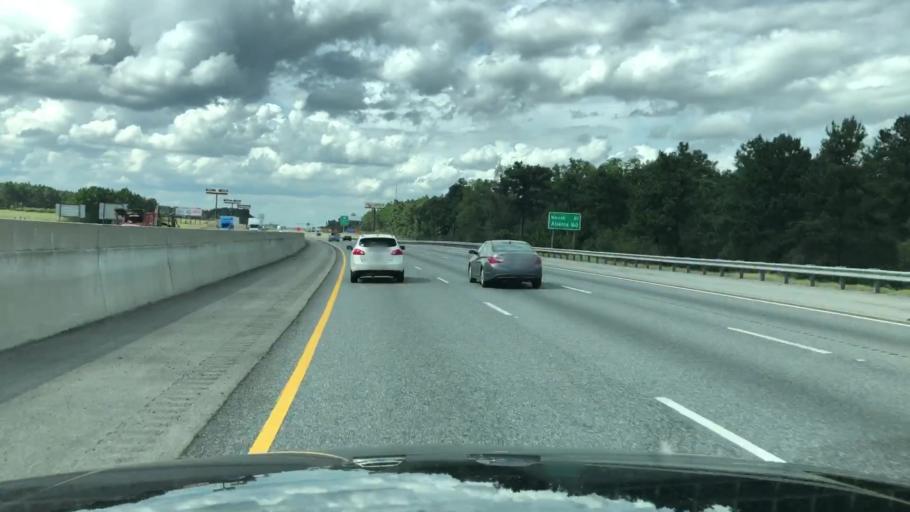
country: US
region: Georgia
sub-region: Turner County
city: Ashburn
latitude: 31.7241
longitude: -83.6432
